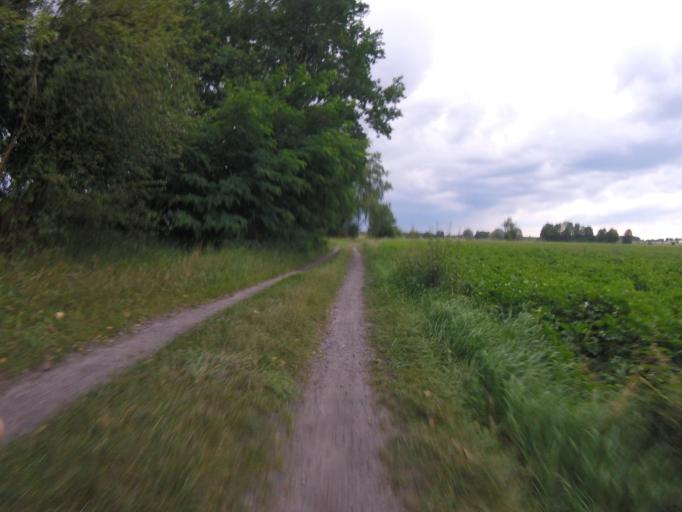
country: DE
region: Brandenburg
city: Mittenwalde
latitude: 52.2719
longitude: 13.5310
